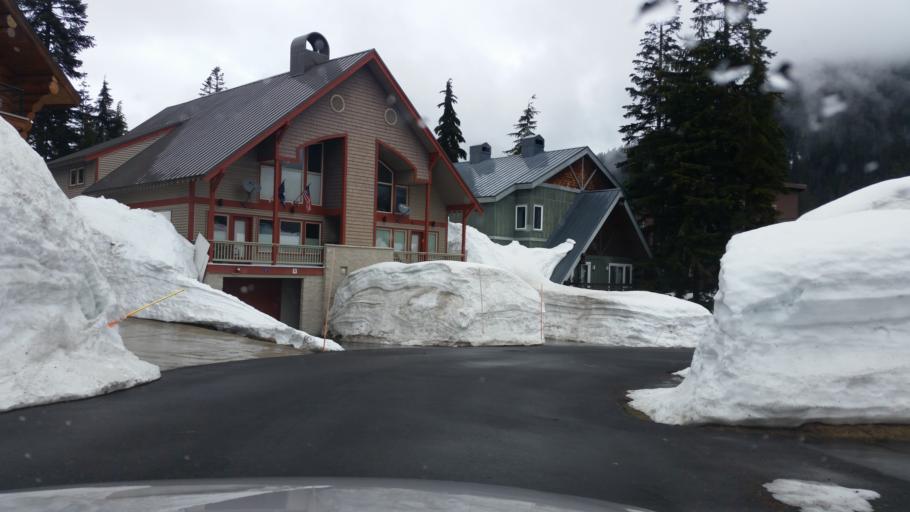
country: US
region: Washington
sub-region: King County
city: Tanner
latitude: 47.4224
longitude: -121.4149
